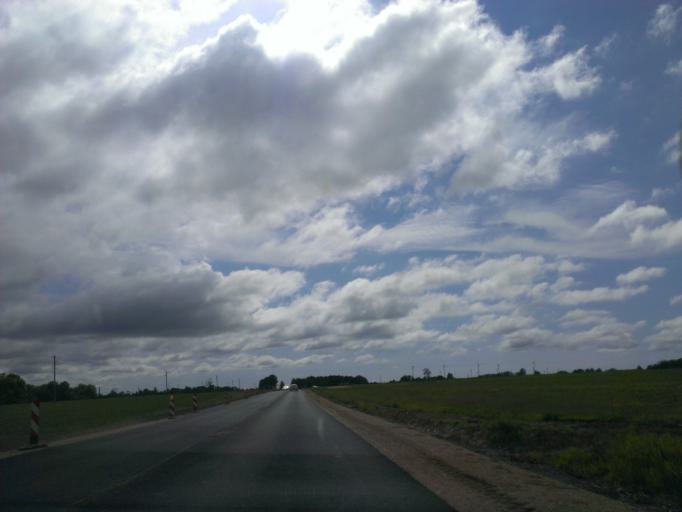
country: LV
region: Durbe
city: Liegi
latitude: 56.5712
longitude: 21.2826
